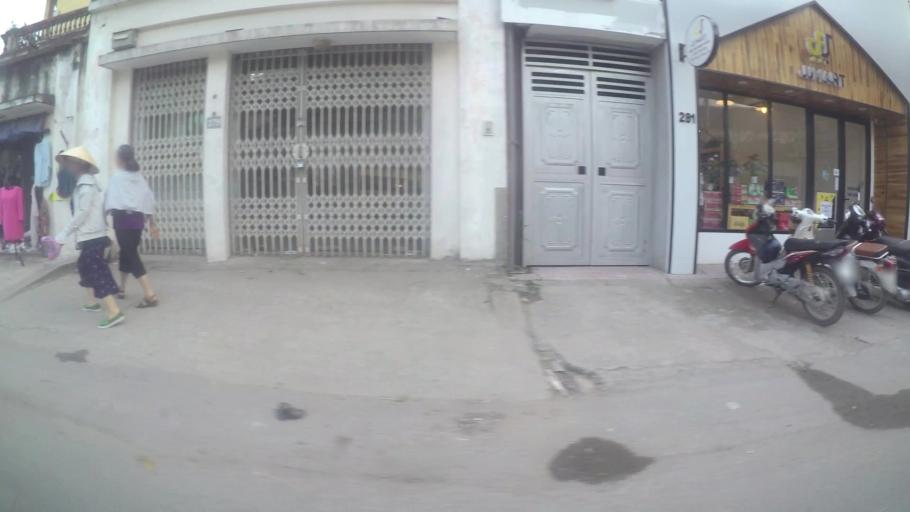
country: VN
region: Ha Noi
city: Tay Ho
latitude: 21.0731
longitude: 105.8021
